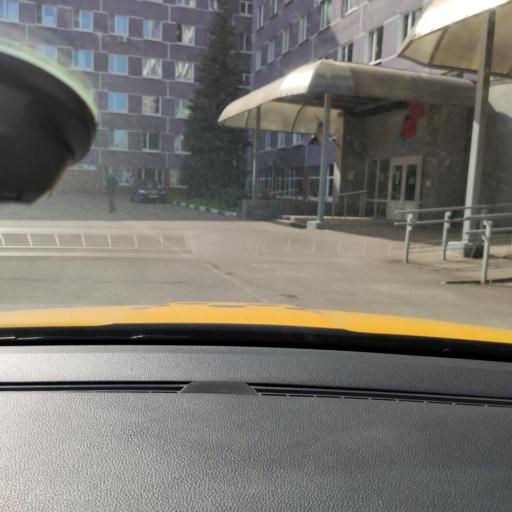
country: RU
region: Moscow
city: Zapadnoye Degunino
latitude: 55.8709
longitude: 37.5267
